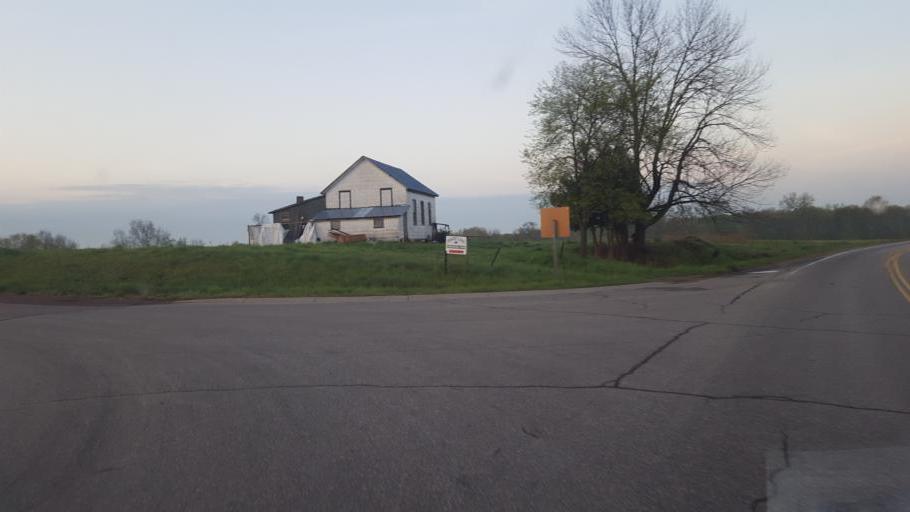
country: US
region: Wisconsin
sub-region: Vernon County
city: Hillsboro
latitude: 43.6186
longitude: -90.4523
